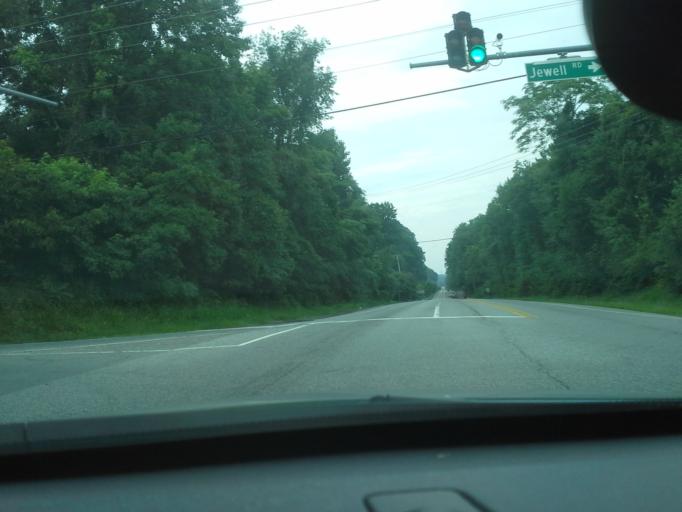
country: US
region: Maryland
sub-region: Calvert County
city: Dunkirk Town Center
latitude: 38.7486
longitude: -76.6396
